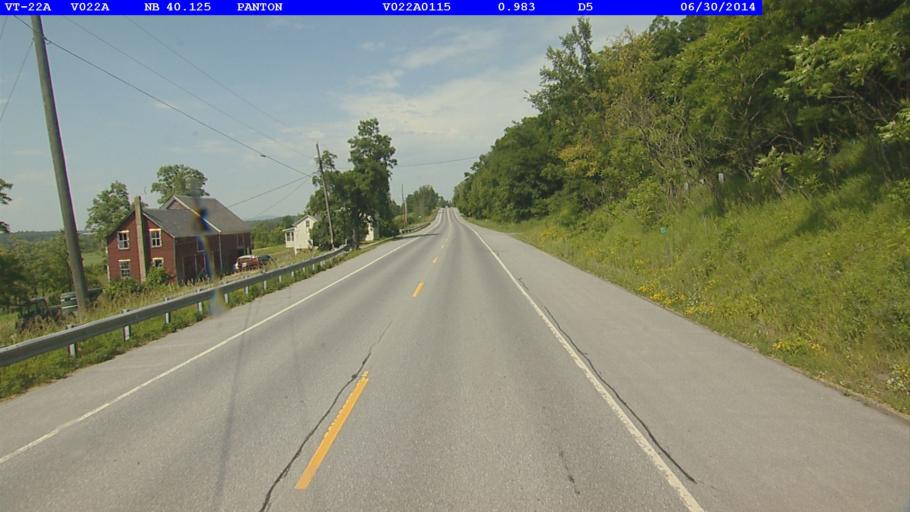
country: US
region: Vermont
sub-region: Addison County
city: Vergennes
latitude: 44.1326
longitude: -73.2859
